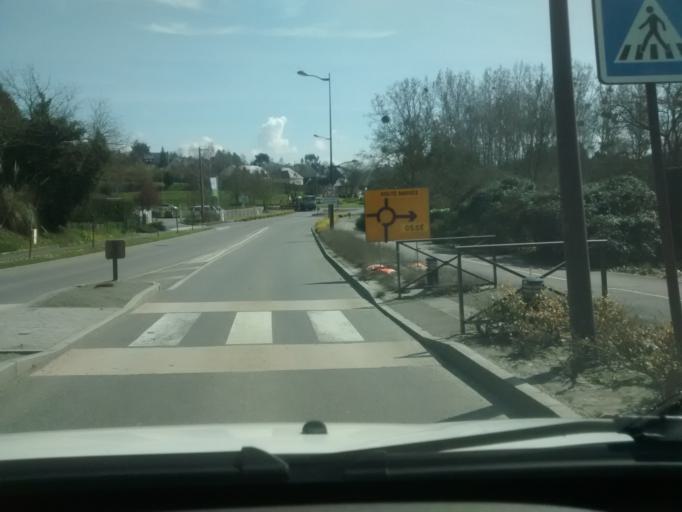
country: FR
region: Brittany
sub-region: Departement d'Ille-et-Vilaine
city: Chateaugiron
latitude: 48.0543
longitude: -1.5135
